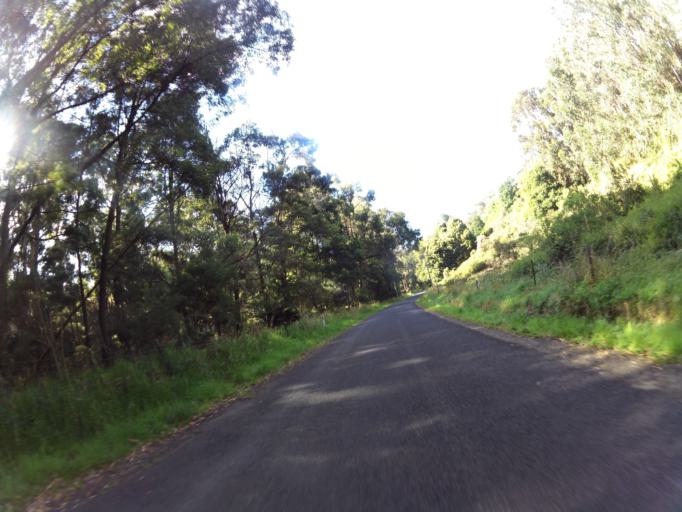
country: AU
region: Victoria
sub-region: Colac-Otway
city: Apollo Bay
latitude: -38.7613
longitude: 143.6301
